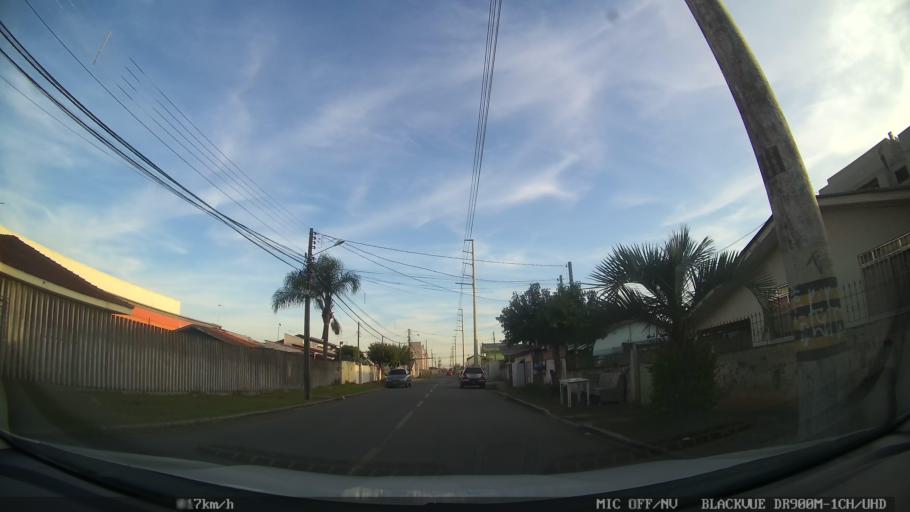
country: BR
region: Parana
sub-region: Pinhais
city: Pinhais
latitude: -25.4457
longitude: -49.1687
